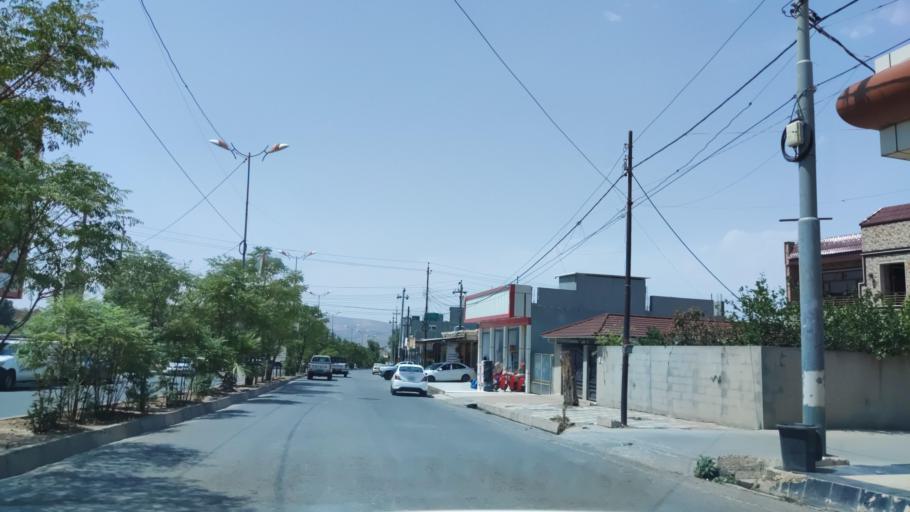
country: IQ
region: Arbil
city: Shaqlawah
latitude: 36.5498
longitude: 44.3535
